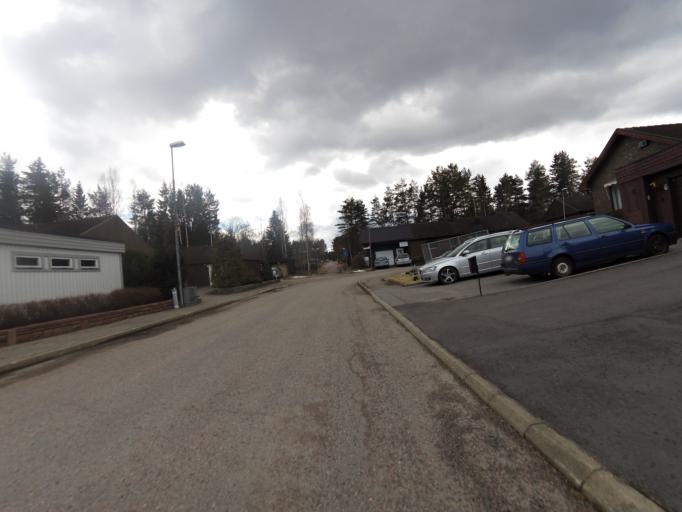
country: SE
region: Gaevleborg
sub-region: Gavle Kommun
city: Gavle
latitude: 60.6907
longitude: 17.0971
